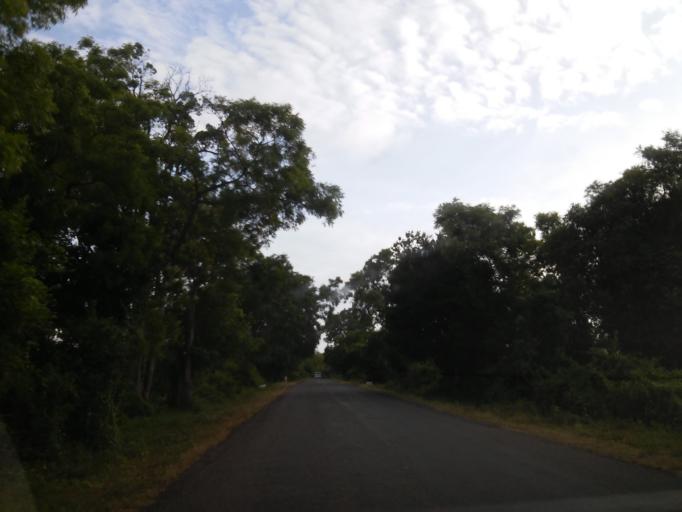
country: LK
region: Central
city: Sigiriya
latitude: 8.1139
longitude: 80.6326
